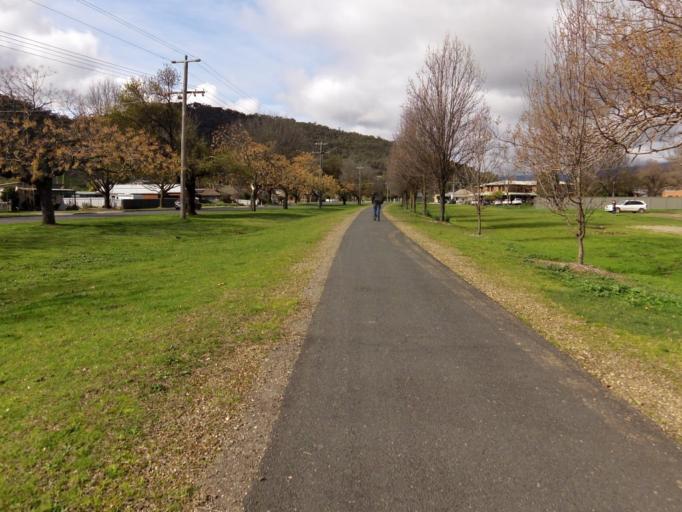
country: AU
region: Victoria
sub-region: Wangaratta
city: Wangaratta
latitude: -36.5611
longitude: 146.7272
